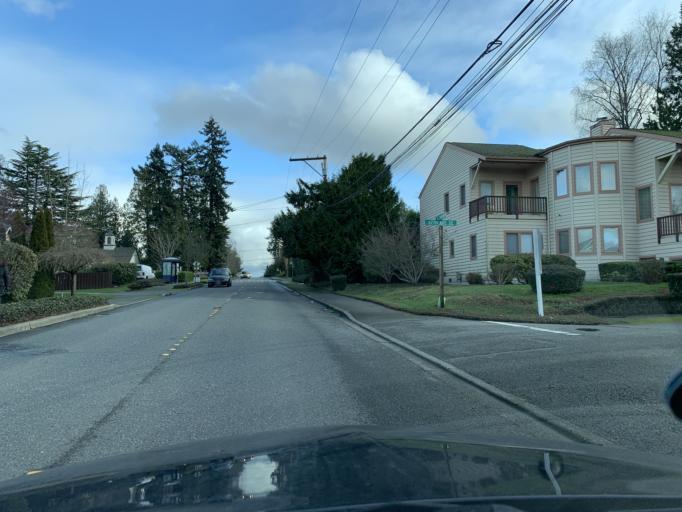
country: US
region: Washington
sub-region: King County
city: Mercer Island
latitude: 47.5891
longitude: -122.2463
